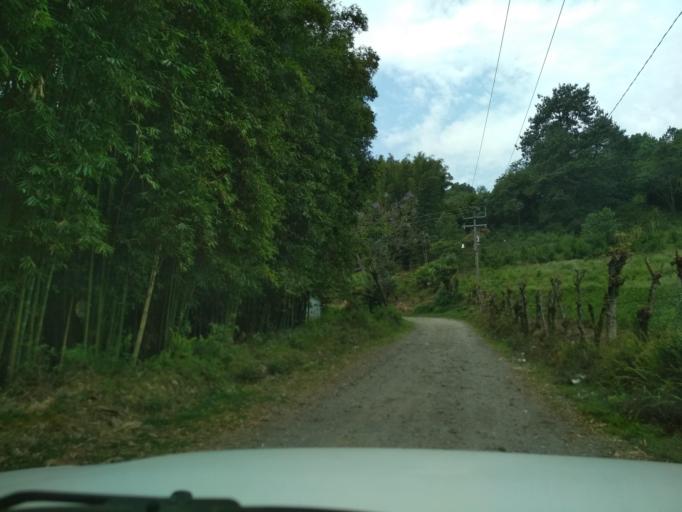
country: MX
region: Veracruz
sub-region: La Perla
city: La Perla
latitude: 18.9230
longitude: -97.1271
